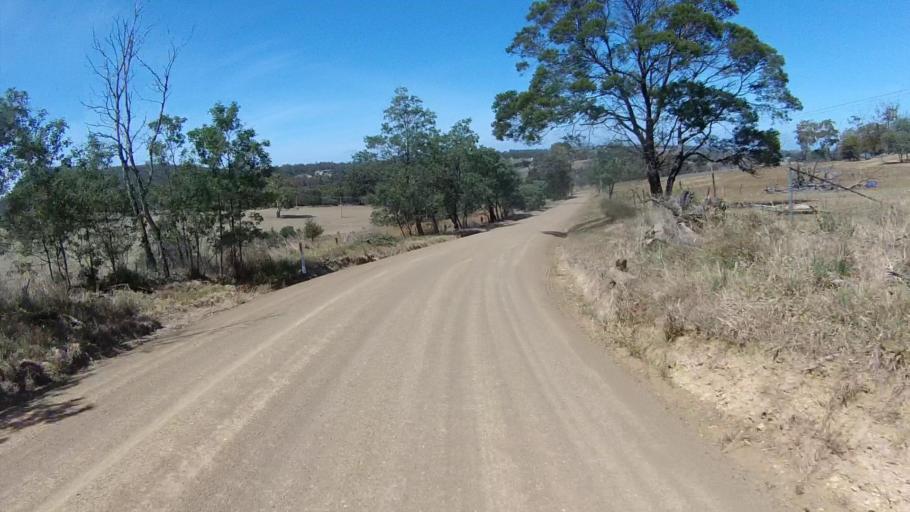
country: AU
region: Tasmania
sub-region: Sorell
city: Sorell
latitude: -42.7957
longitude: 147.6406
